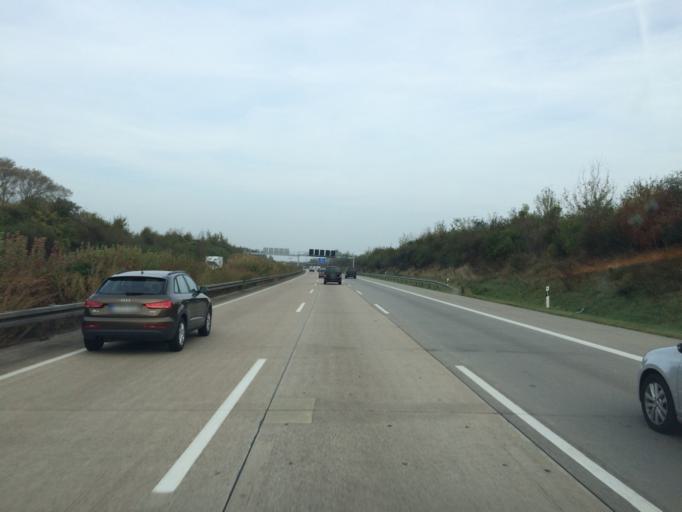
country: DE
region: Lower Saxony
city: Isernhagen Farster Bauerschaft
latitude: 52.4758
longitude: 9.8529
